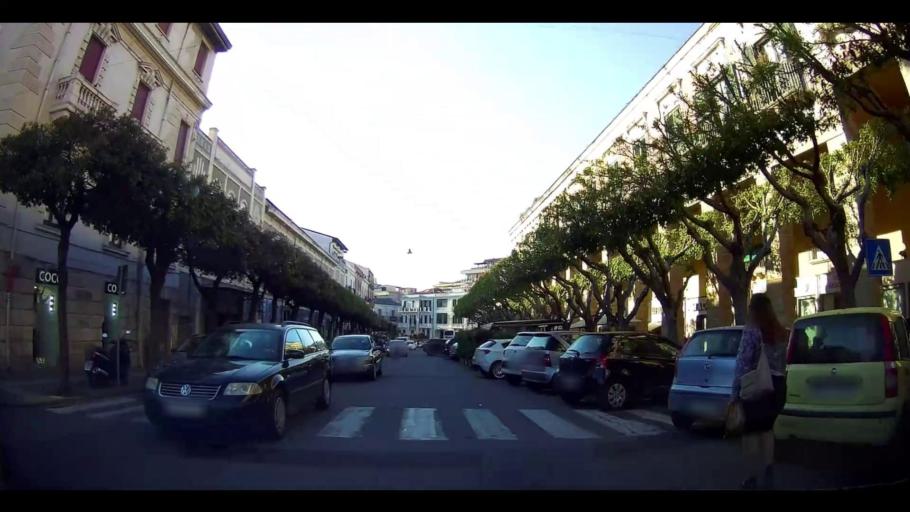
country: IT
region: Calabria
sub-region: Provincia di Crotone
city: Crotone
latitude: 39.0812
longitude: 17.1268
